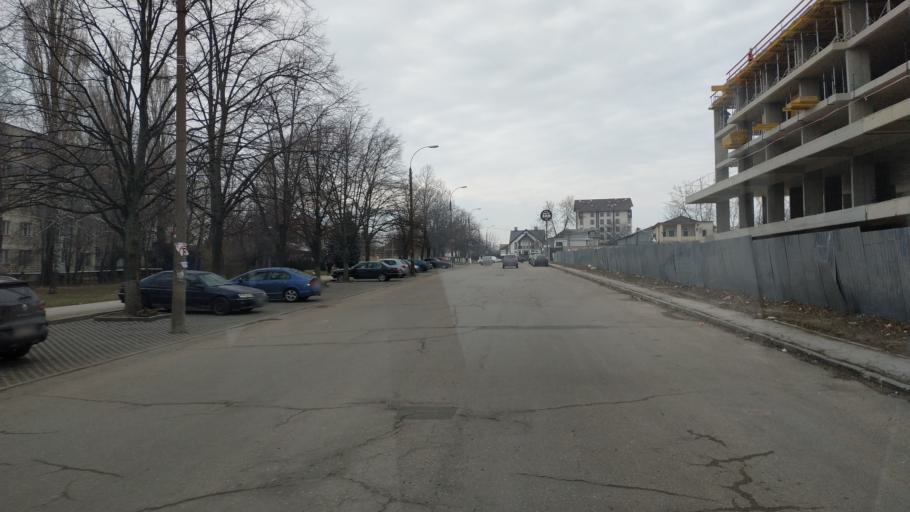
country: MD
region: Chisinau
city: Vatra
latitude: 47.0346
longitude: 28.7750
